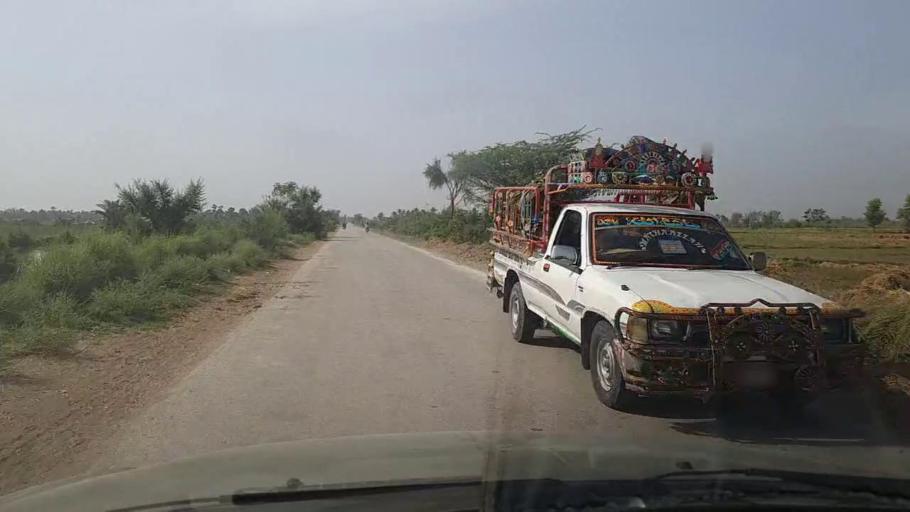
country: PK
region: Sindh
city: Gambat
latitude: 27.4494
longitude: 68.4861
